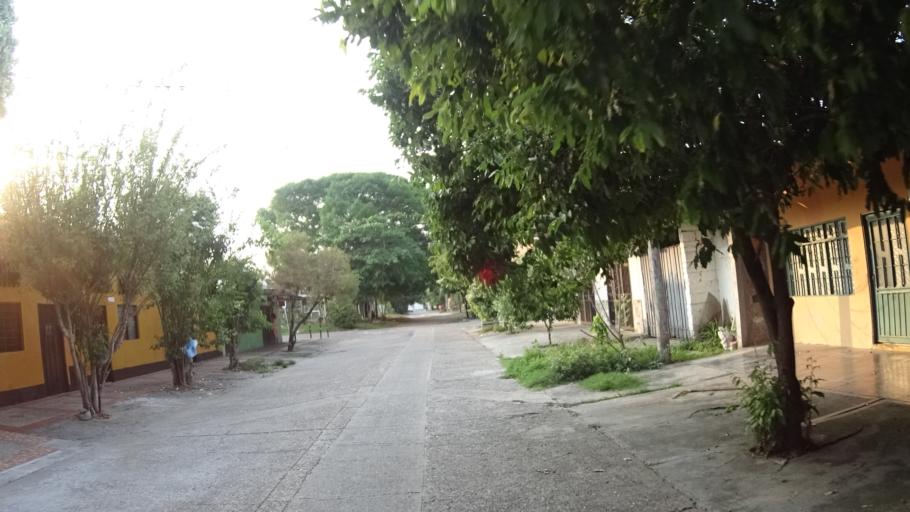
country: CO
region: Caldas
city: La Dorada
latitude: 5.4456
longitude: -74.6600
